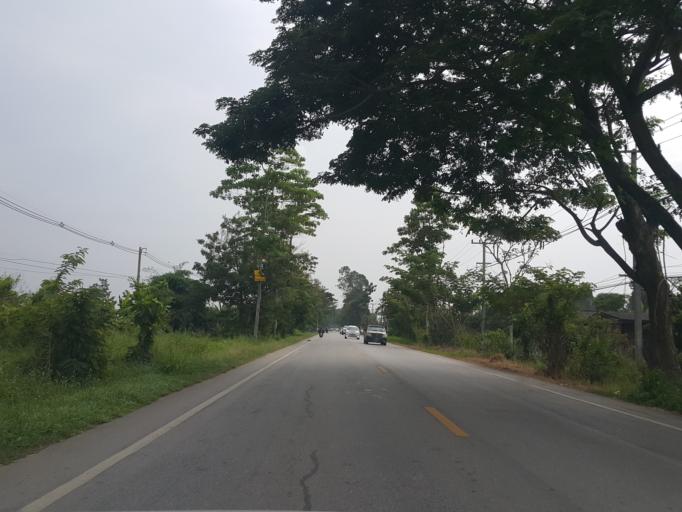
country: TH
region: Chiang Mai
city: Mae Taeng
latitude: 19.0192
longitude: 98.9697
